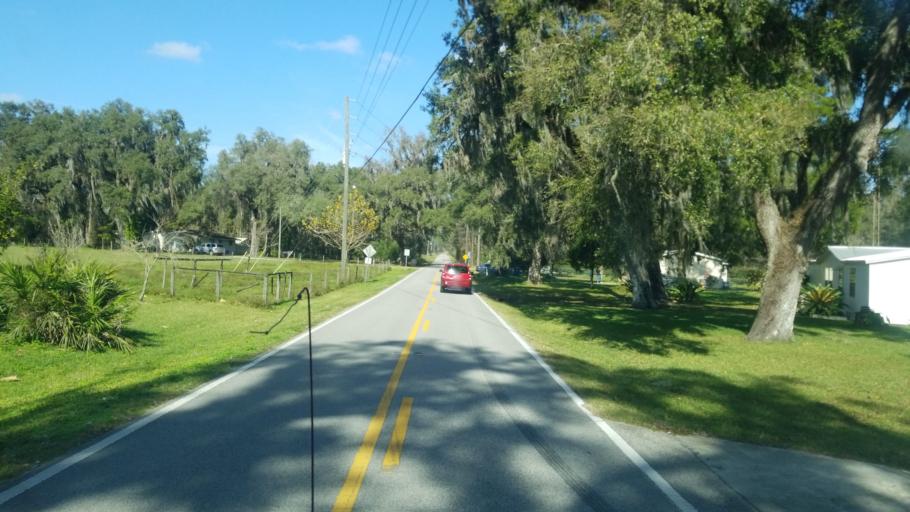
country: US
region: Florida
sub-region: Hernando County
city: North Brooksville
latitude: 28.5955
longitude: -82.3761
